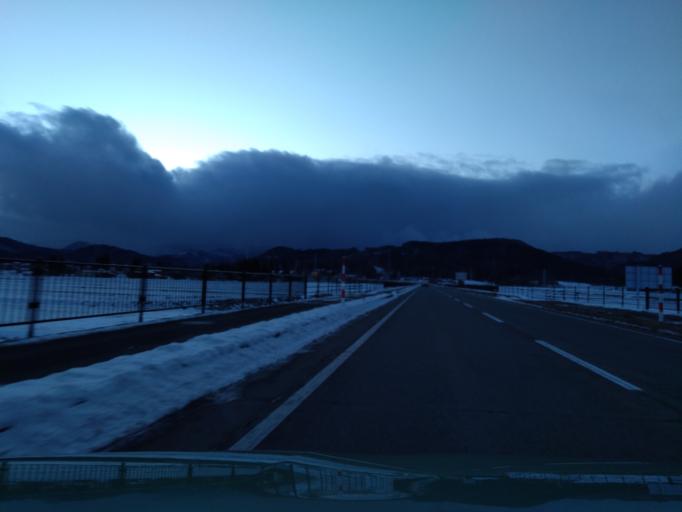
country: JP
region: Iwate
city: Shizukuishi
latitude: 39.6977
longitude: 140.9449
